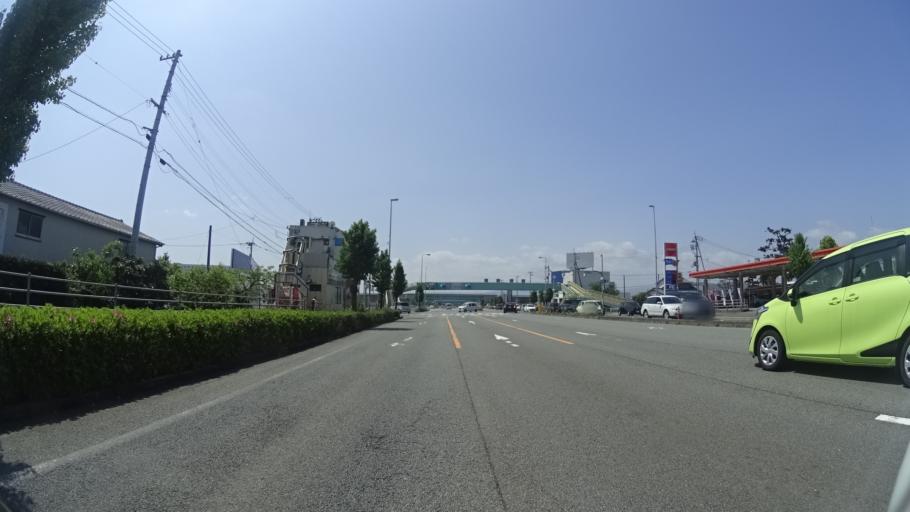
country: JP
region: Tokushima
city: Tokushima-shi
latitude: 34.1063
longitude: 134.5764
